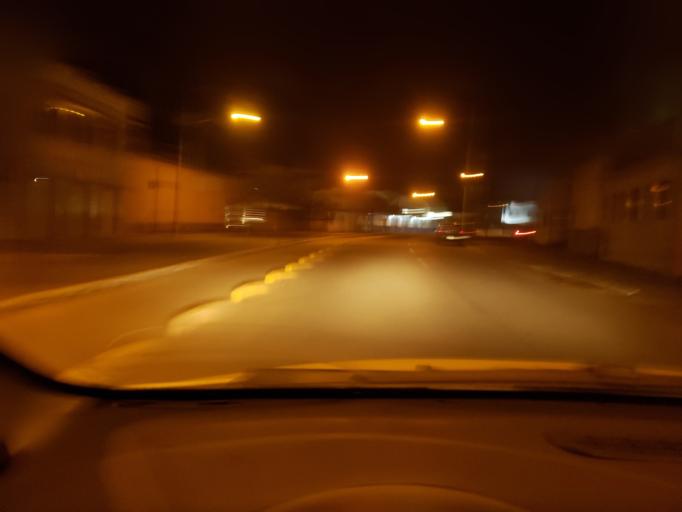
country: BR
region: Minas Gerais
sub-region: Campo Belo
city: Campo Belo
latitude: -20.8944
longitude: -45.2696
